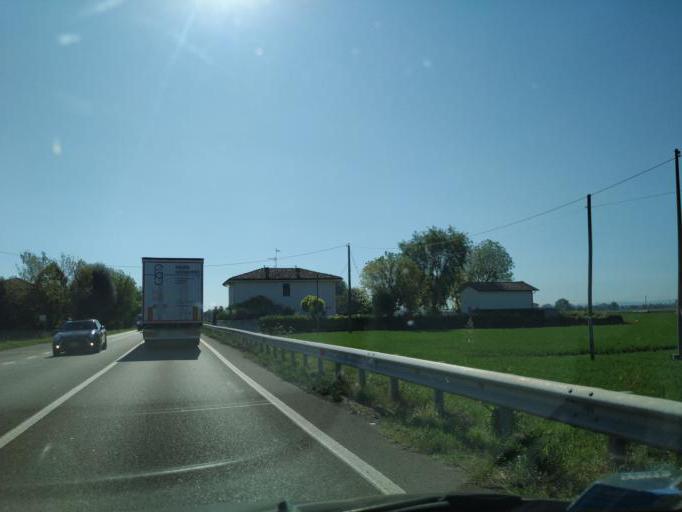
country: IT
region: Emilia-Romagna
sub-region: Provincia di Bologna
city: Sant'Agata Bolognese
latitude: 44.6510
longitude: 11.1532
